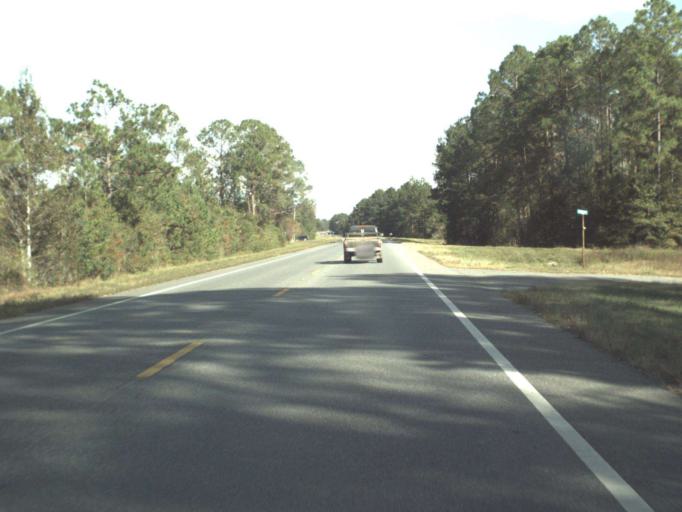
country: US
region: Florida
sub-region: Washington County
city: Chipley
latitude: 30.7778
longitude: -85.6055
